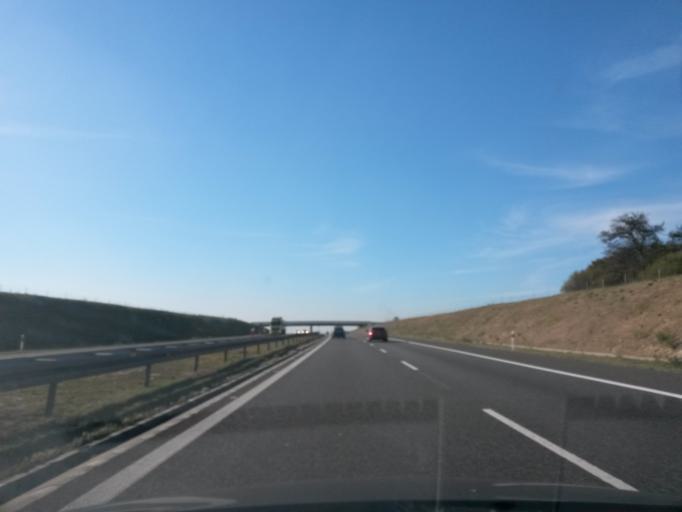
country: PL
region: Opole Voivodeship
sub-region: Powiat krapkowicki
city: Gogolin
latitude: 50.4816
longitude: 18.0554
